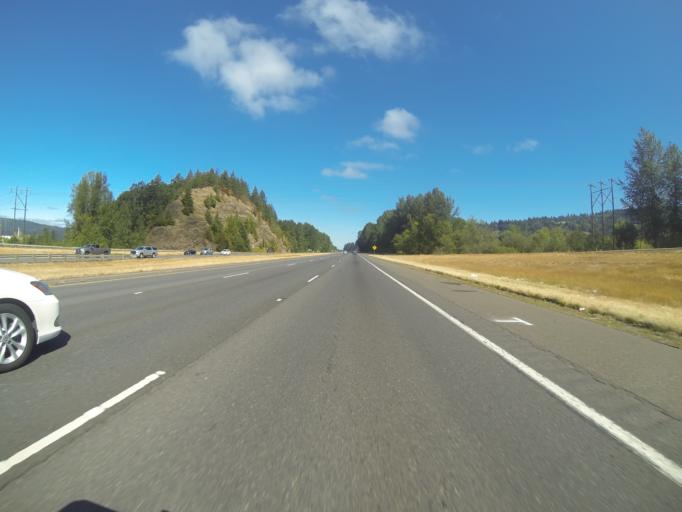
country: US
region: Washington
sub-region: Cowlitz County
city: Kalama
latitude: 46.0422
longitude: -122.8591
